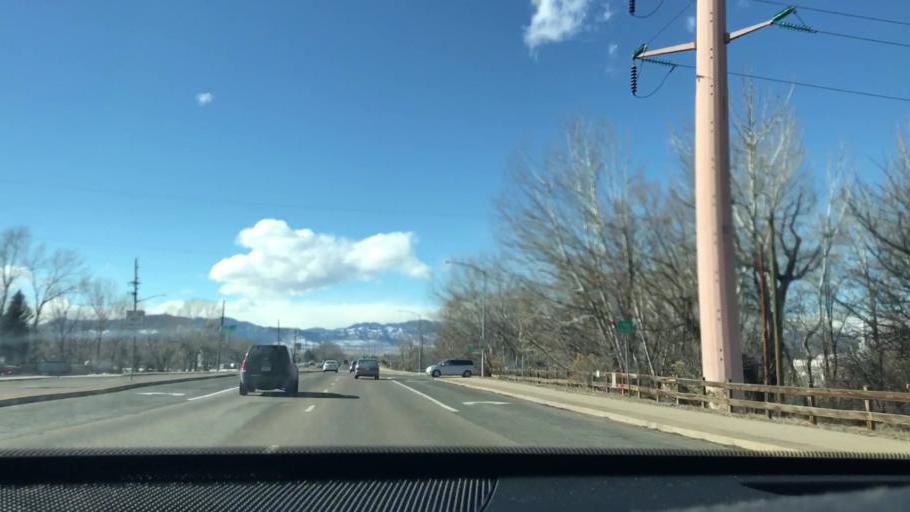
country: US
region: Colorado
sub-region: Adams County
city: Westminster
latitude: 39.8638
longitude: -105.0717
